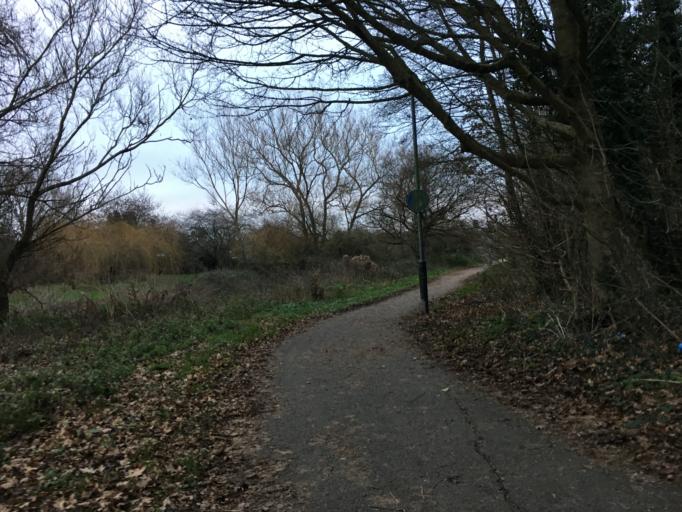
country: GB
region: England
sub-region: Warwickshire
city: Rugby
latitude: 52.3641
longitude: -1.2652
